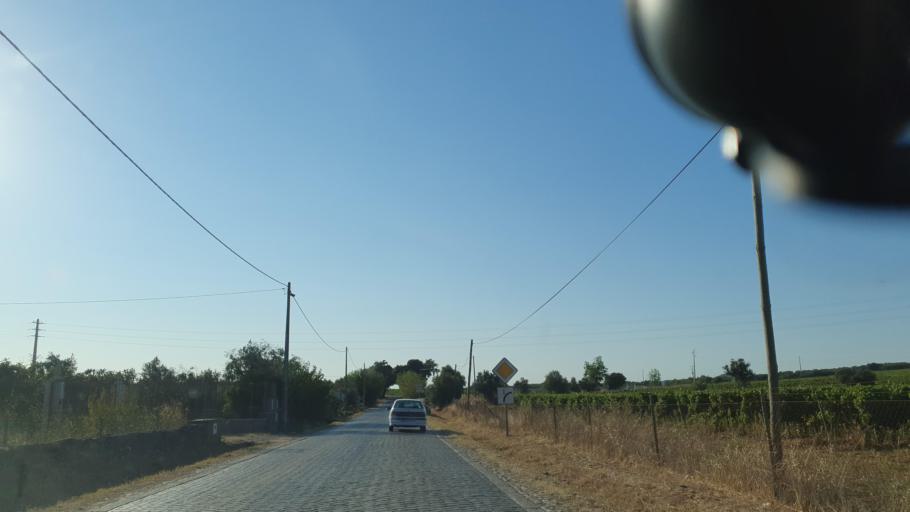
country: PT
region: Evora
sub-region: Estremoz
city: Estremoz
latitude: 38.8494
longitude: -7.6098
